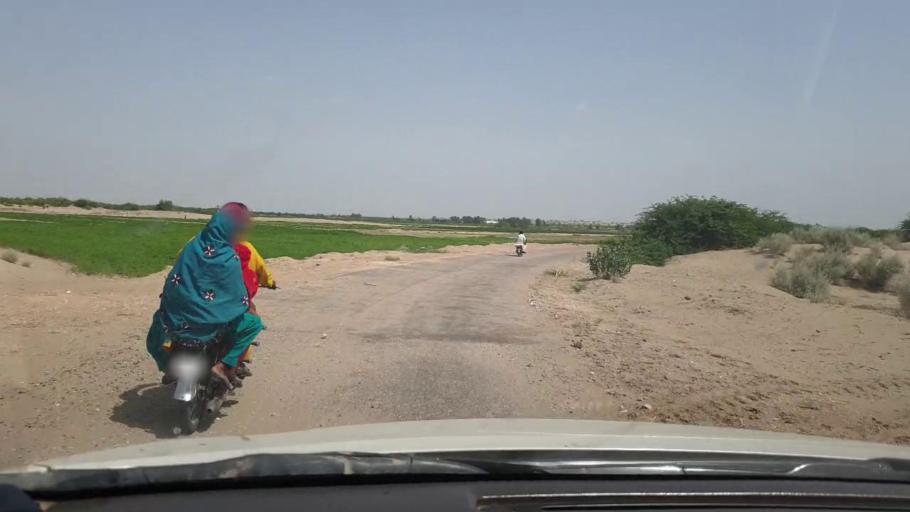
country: PK
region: Sindh
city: Rohri
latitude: 27.4892
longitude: 69.0530
